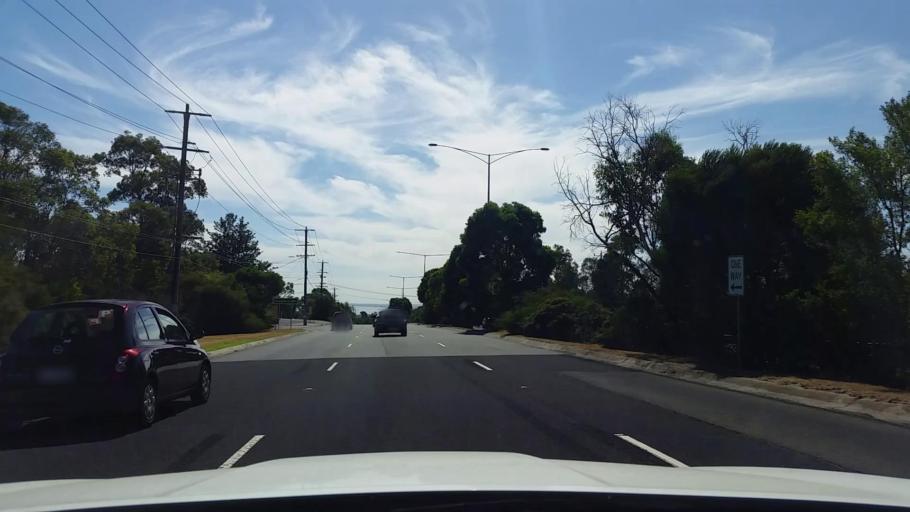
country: AU
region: Victoria
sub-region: Frankston
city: Frankston South
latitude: -38.1726
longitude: 145.1391
